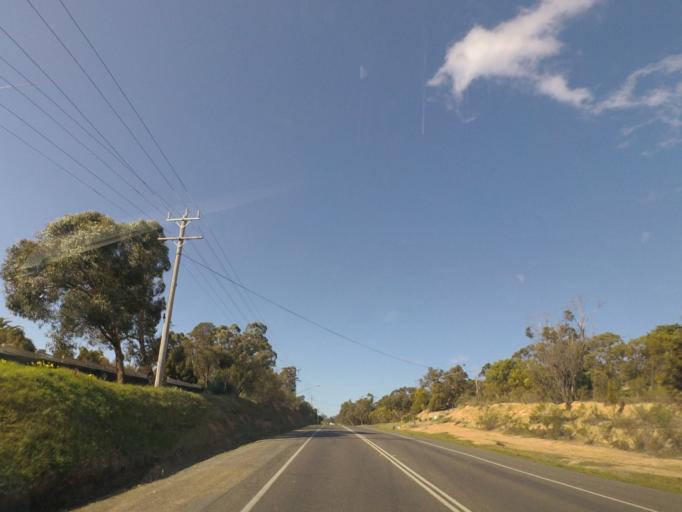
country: AU
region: Victoria
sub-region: Manningham
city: Park Orchards
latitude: -37.7658
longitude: 145.1905
